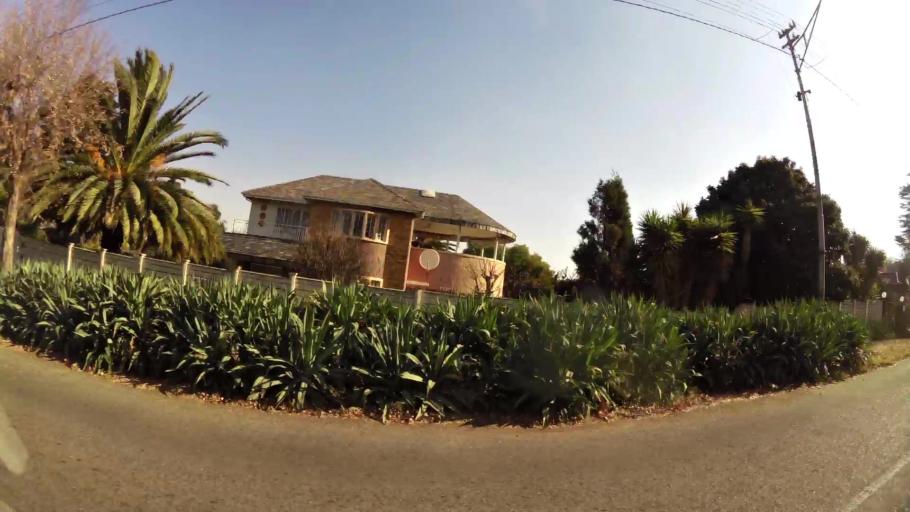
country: ZA
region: Gauteng
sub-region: City of Johannesburg Metropolitan Municipality
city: Johannesburg
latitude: -26.1720
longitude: 28.1049
